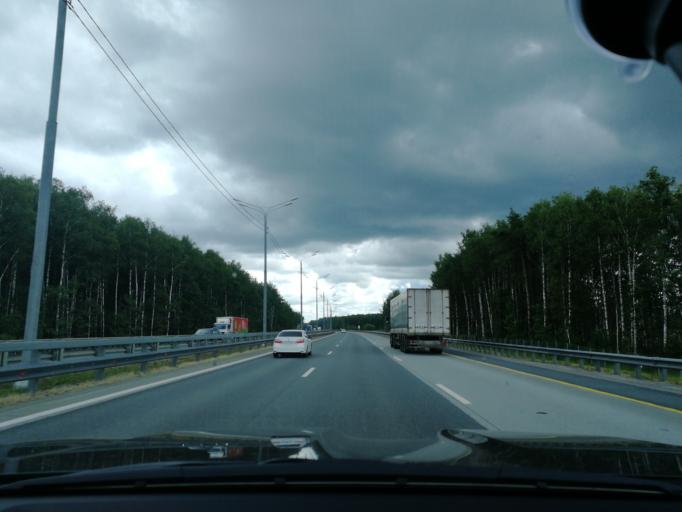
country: RU
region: Moskovskaya
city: Barybino
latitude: 55.2217
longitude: 37.8747
